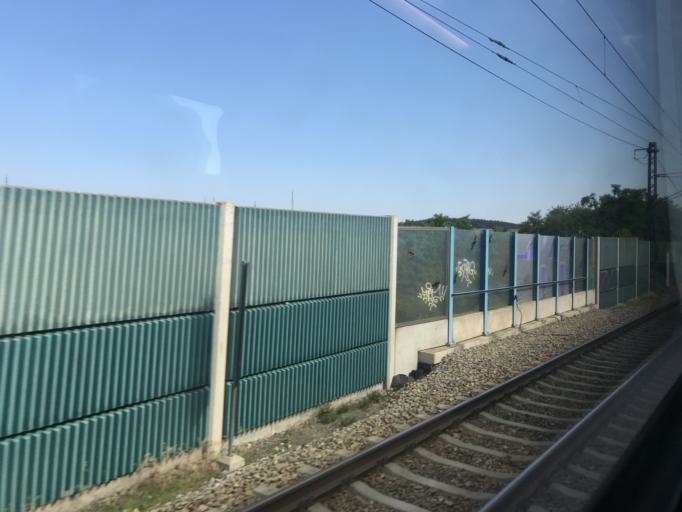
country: CZ
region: Central Bohemia
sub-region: Okres Benesov
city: Benesov
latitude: 49.7926
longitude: 14.6969
